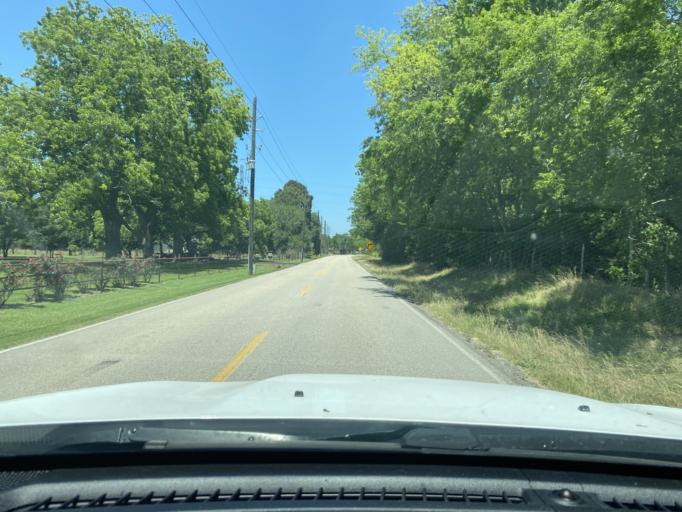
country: US
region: Texas
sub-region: Waller County
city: Waller
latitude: 30.0197
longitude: -95.8487
